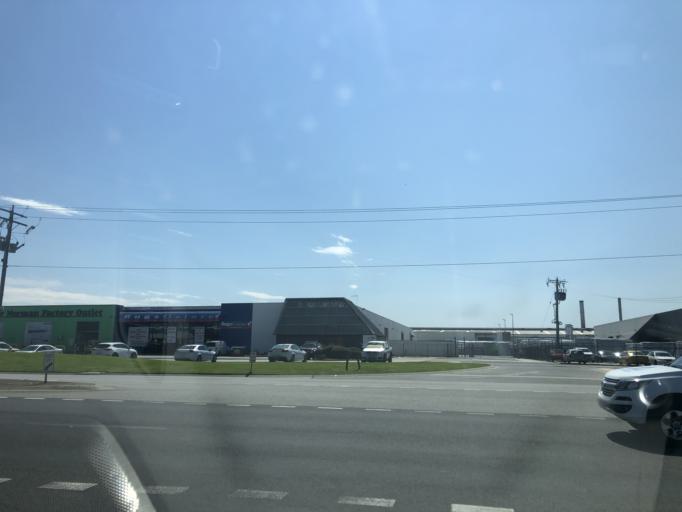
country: AU
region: Victoria
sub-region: Casey
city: Doveton
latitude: -38.0151
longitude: 145.2182
